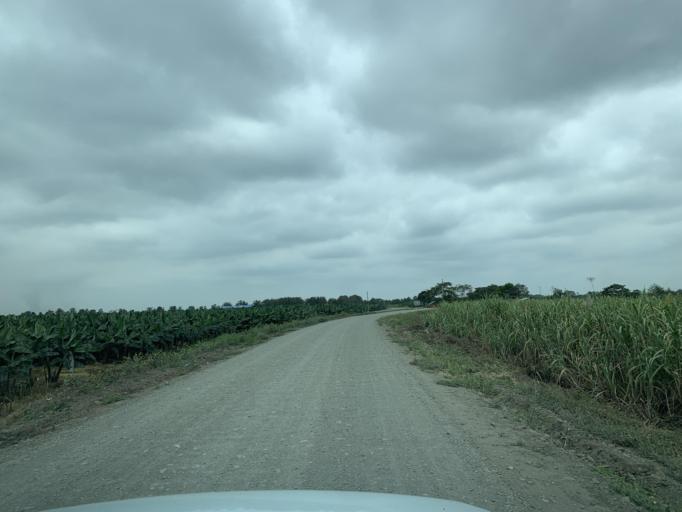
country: EC
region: Guayas
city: Coronel Marcelino Mariduena
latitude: -2.3293
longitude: -79.4549
